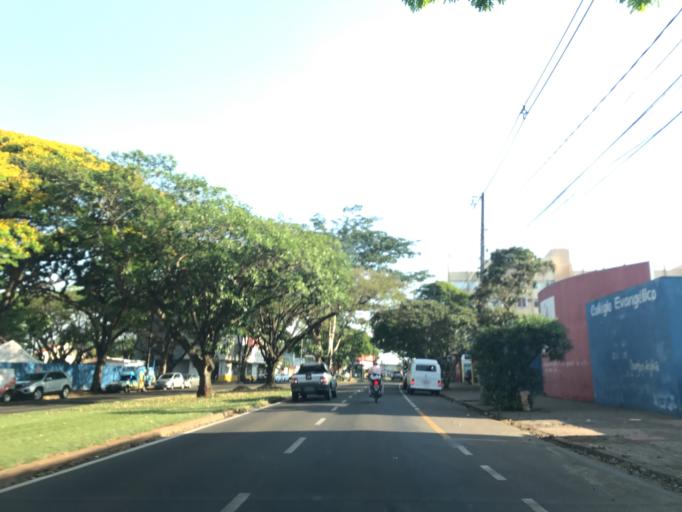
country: BR
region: Parana
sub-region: Maringa
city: Maringa
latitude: -23.4306
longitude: -51.9526
